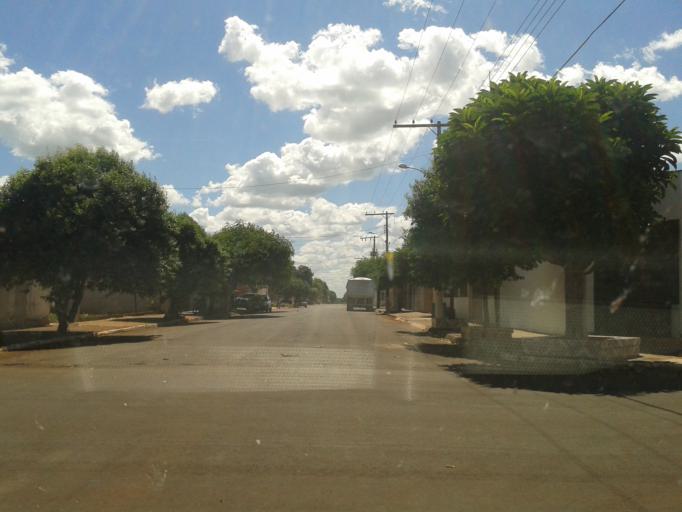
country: BR
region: Minas Gerais
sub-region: Santa Vitoria
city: Santa Vitoria
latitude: -18.6952
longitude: -49.9469
